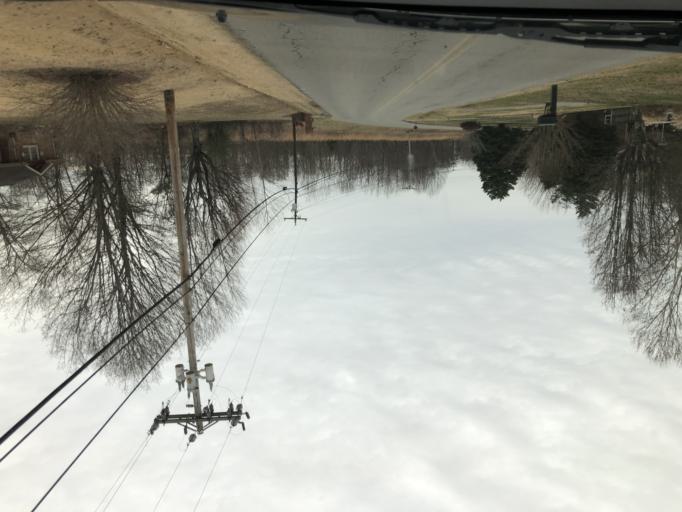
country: US
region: Tennessee
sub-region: Sumner County
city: White House
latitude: 36.4262
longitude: -86.6896
